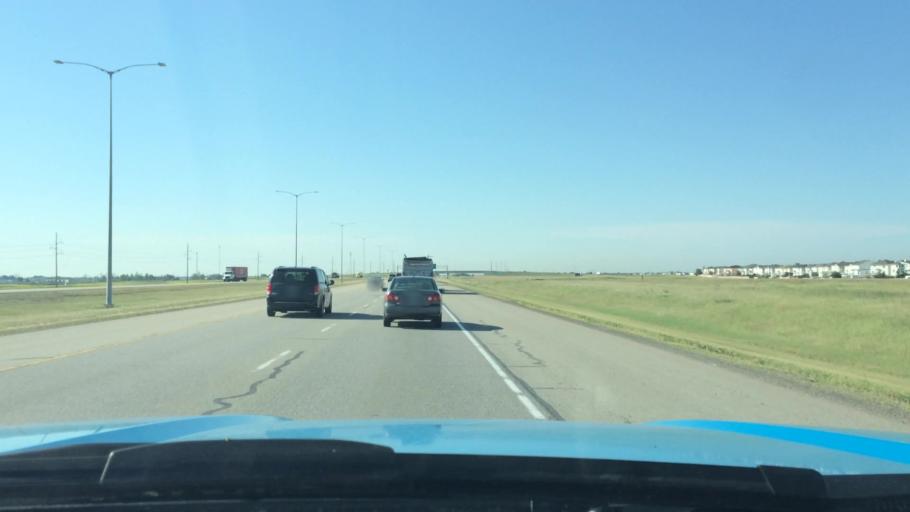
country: CA
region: Alberta
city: Chestermere
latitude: 51.1101
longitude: -113.9206
